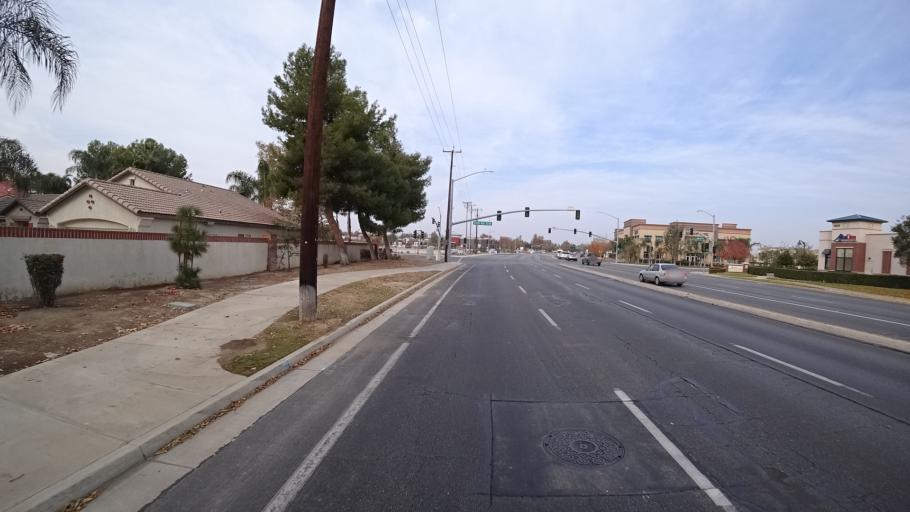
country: US
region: California
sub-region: Kern County
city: Rosedale
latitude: 35.3463
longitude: -119.1281
